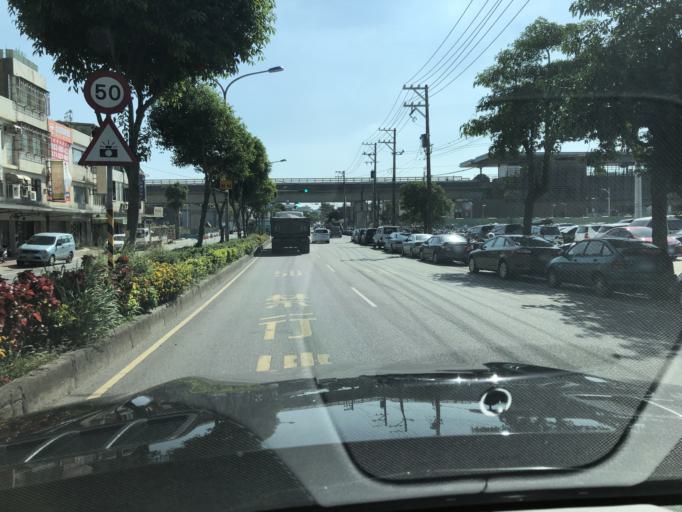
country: TW
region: Taiwan
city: Taoyuan City
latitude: 25.0821
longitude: 121.2859
